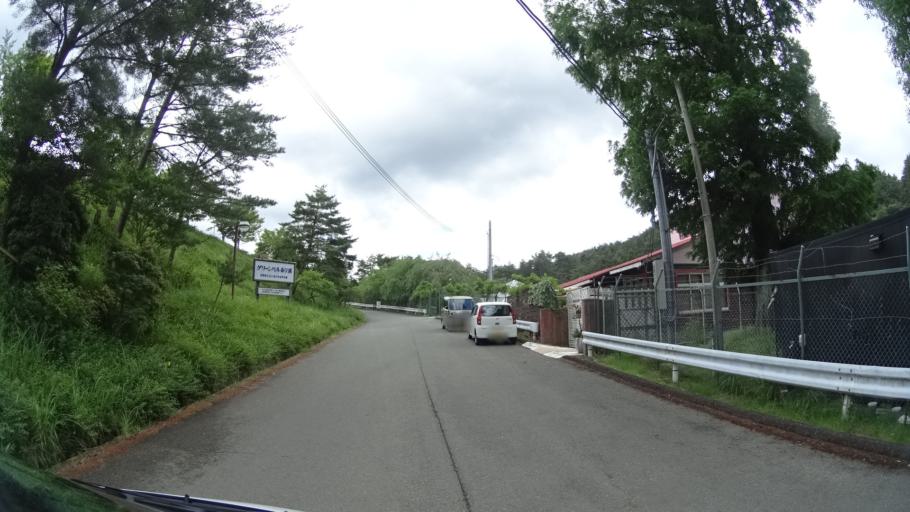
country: JP
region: Hyogo
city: Sasayama
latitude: 35.0299
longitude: 135.3988
